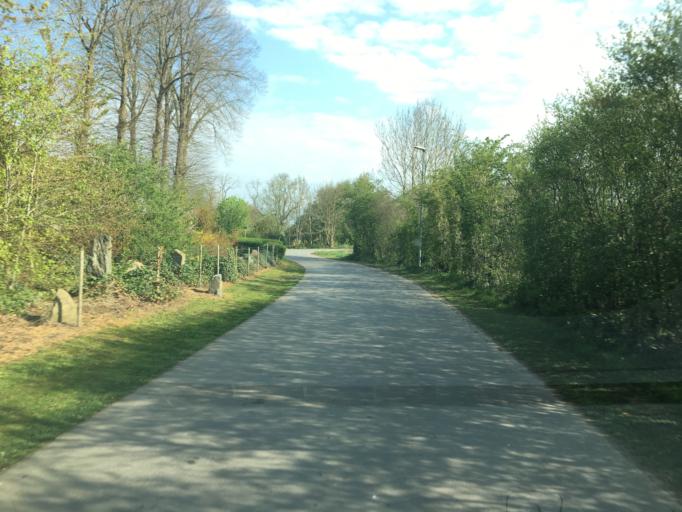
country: DK
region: South Denmark
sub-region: Haderslev Kommune
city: Vojens
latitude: 55.1676
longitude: 9.3806
